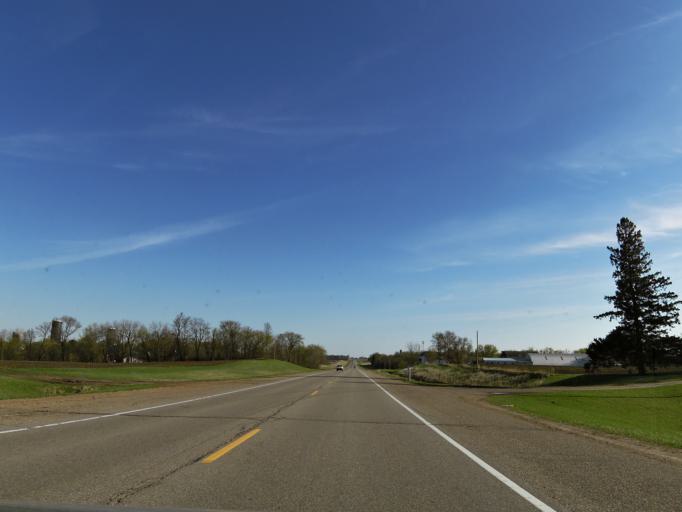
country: US
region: Minnesota
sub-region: Le Sueur County
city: New Prague
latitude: 44.6254
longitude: -93.5017
